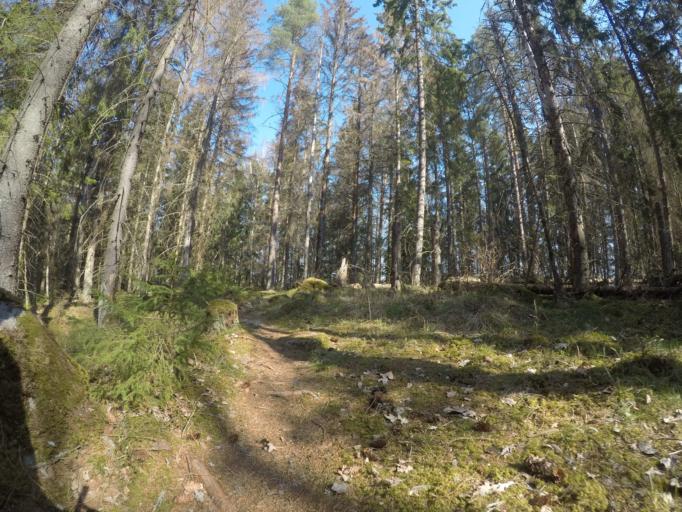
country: SE
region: Vaestmanland
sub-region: Hallstahammars Kommun
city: Kolback
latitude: 59.5359
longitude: 16.2808
